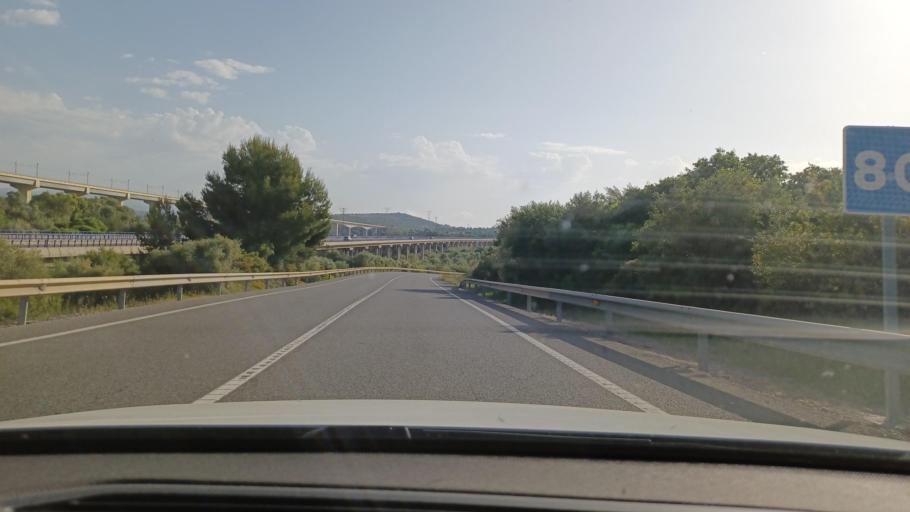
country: ES
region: Catalonia
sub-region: Provincia de Tarragona
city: Amposta
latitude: 40.7233
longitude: 0.5668
